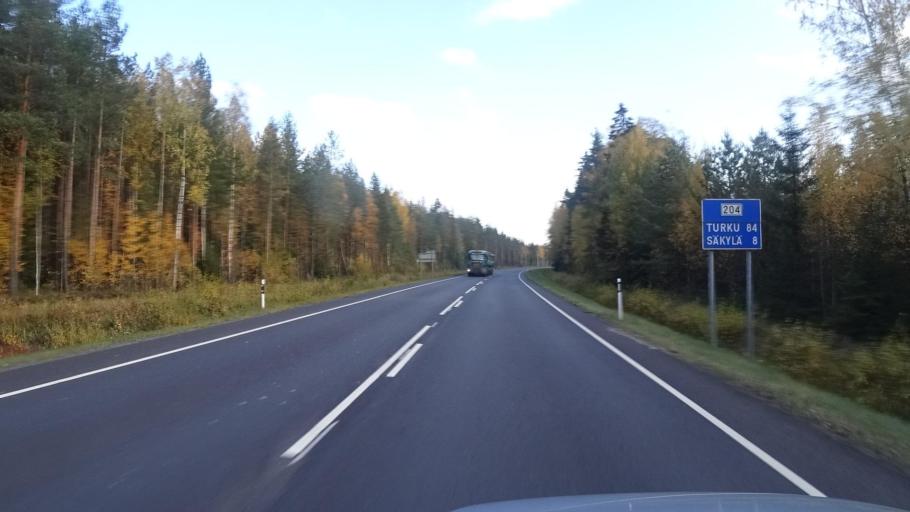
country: FI
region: Satakunta
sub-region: Rauma
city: Koeylioe
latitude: 61.1044
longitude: 22.2283
